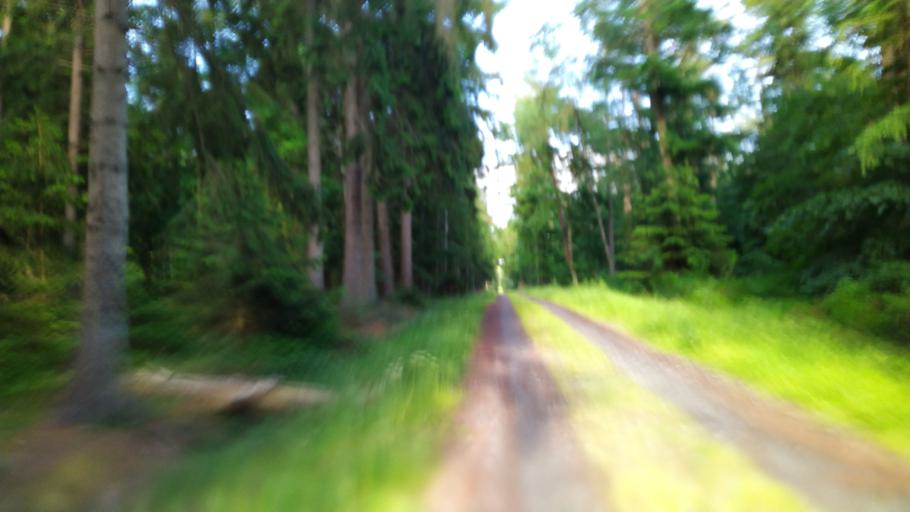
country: DE
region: Lower Saxony
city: Deinstedt
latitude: 53.4389
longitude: 9.2381
